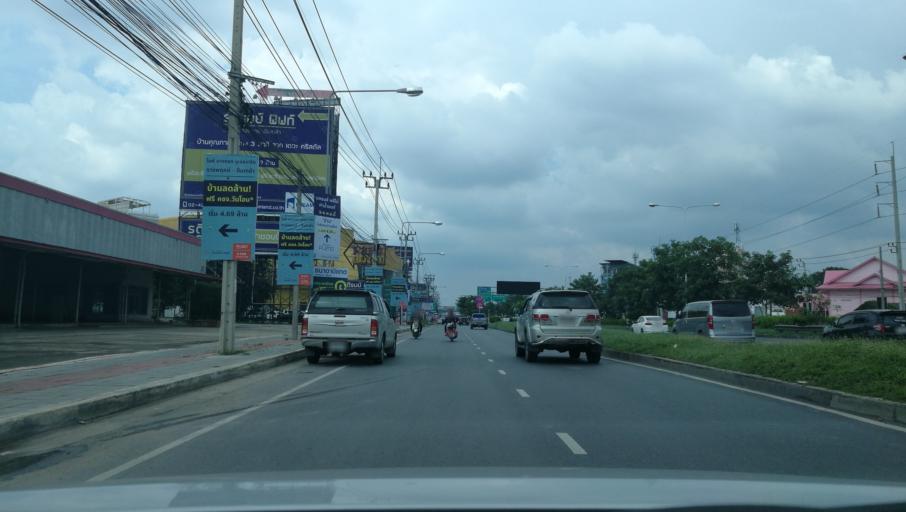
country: TH
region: Nonthaburi
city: Bang Kruai
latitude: 13.8141
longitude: 100.4493
